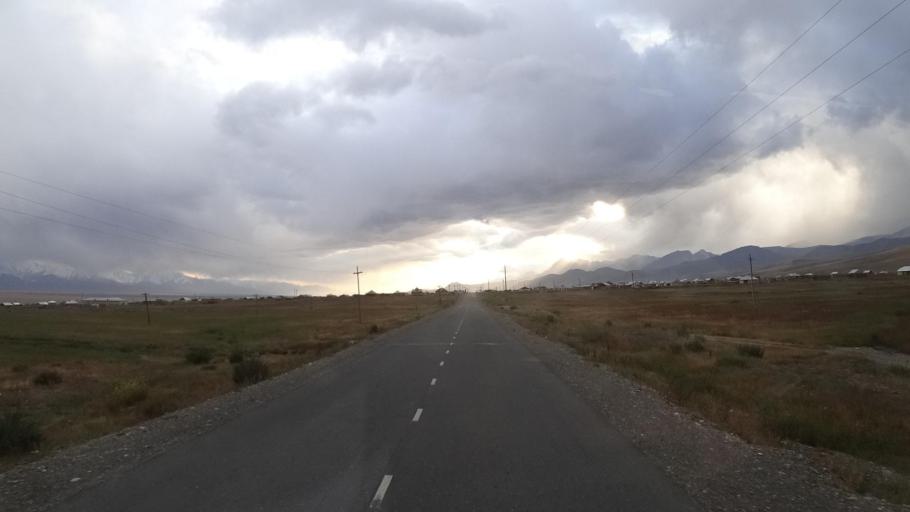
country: KG
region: Osh
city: Gul'cha
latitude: 39.6785
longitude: 72.8969
